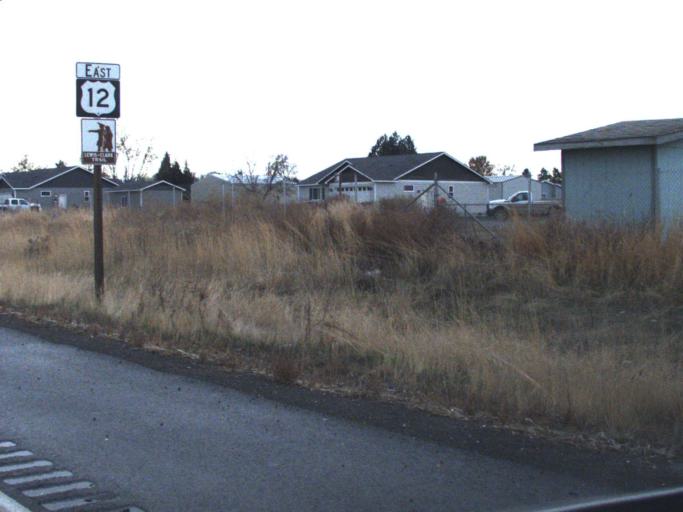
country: US
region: Washington
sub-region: Walla Walla County
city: Burbank
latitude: 46.1964
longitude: -118.9948
